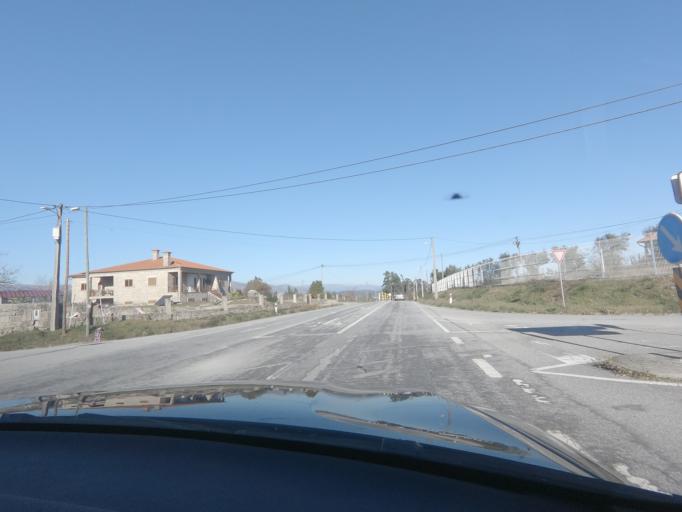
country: PT
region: Viseu
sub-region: Vouzela
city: Vouzela
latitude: 40.7169
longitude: -8.1345
